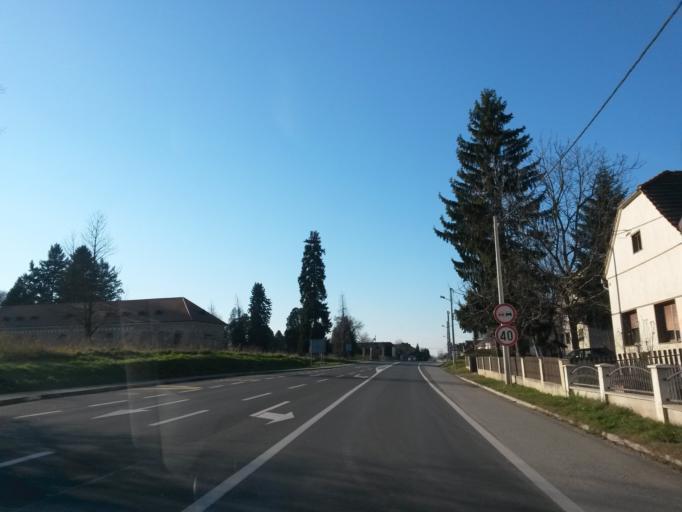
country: HR
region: Varazdinska
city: Jalzabet
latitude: 46.2642
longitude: 16.5416
